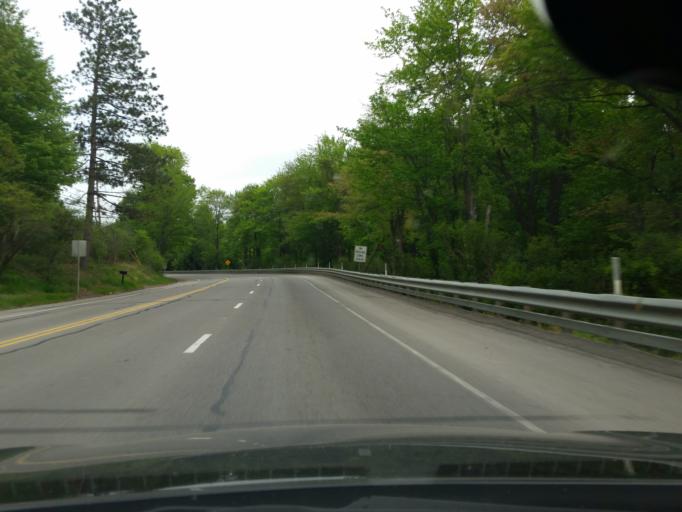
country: US
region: Pennsylvania
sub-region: Elk County
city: Ridgway
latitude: 41.4149
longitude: -78.7150
